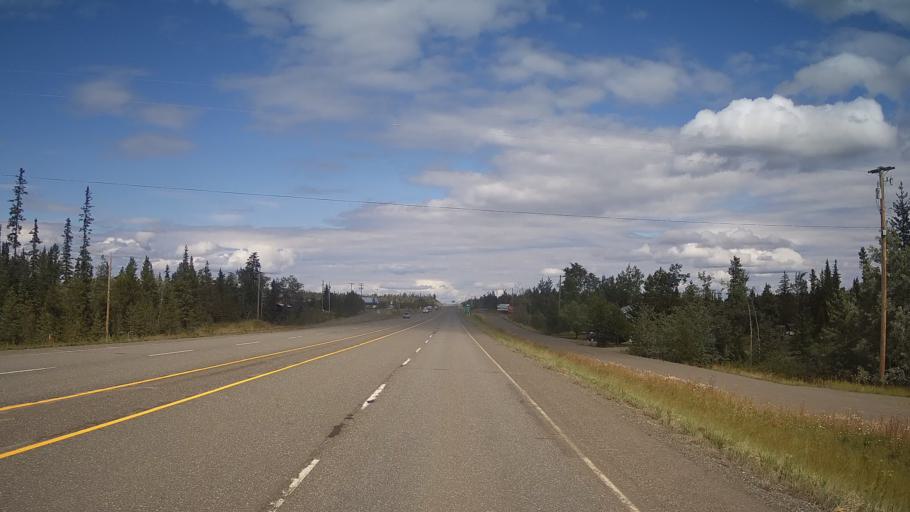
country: CA
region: British Columbia
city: Cache Creek
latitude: 51.5719
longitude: -121.3416
